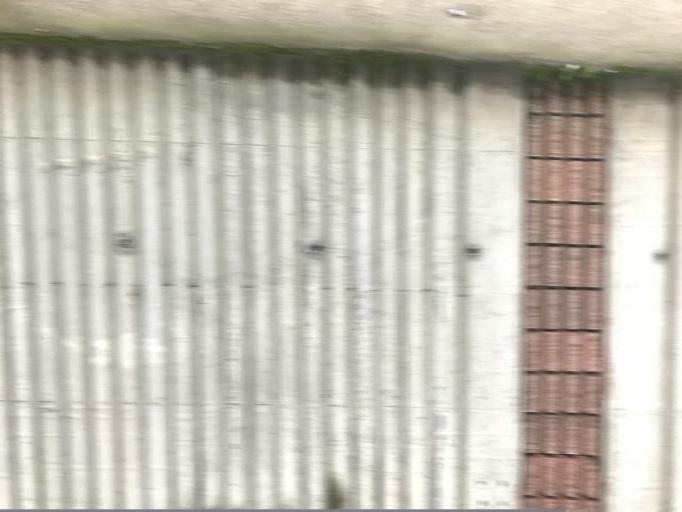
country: TR
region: Istanbul
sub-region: Atasehir
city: Atasehir
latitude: 40.9898
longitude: 29.1047
